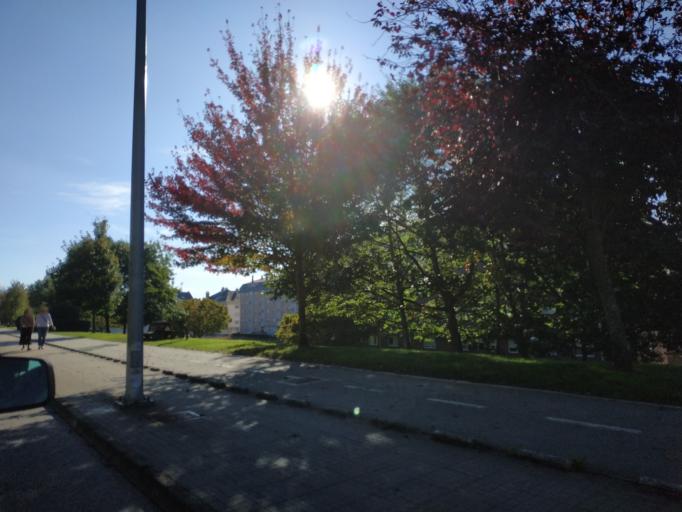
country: ES
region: Galicia
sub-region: Provincia de Lugo
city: Lugo
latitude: 43.0002
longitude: -7.5541
